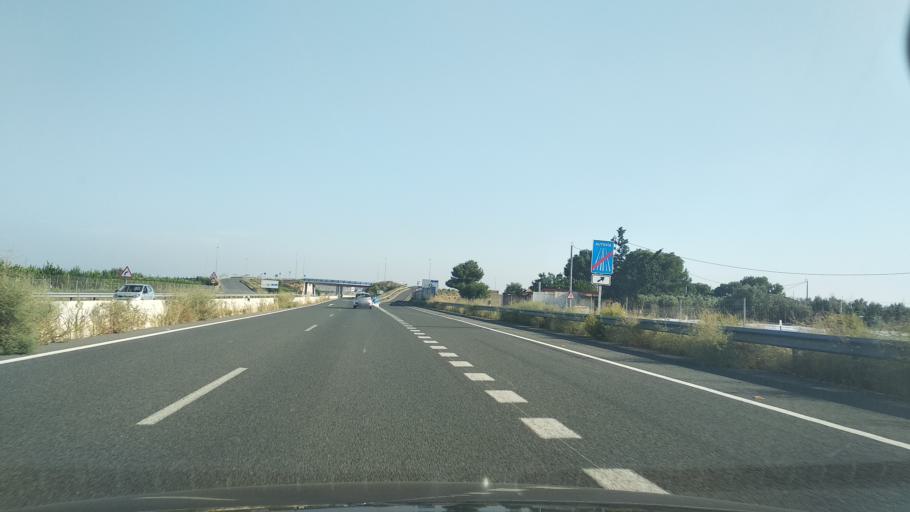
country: ES
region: Murcia
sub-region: Murcia
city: San Javier
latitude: 37.8517
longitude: -0.8798
